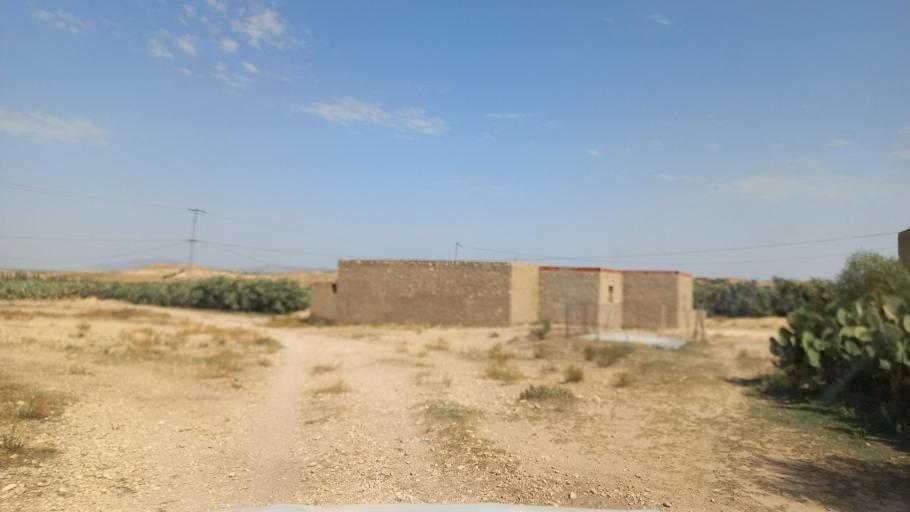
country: TN
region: Al Qasrayn
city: Kasserine
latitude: 35.2784
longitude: 8.9665
